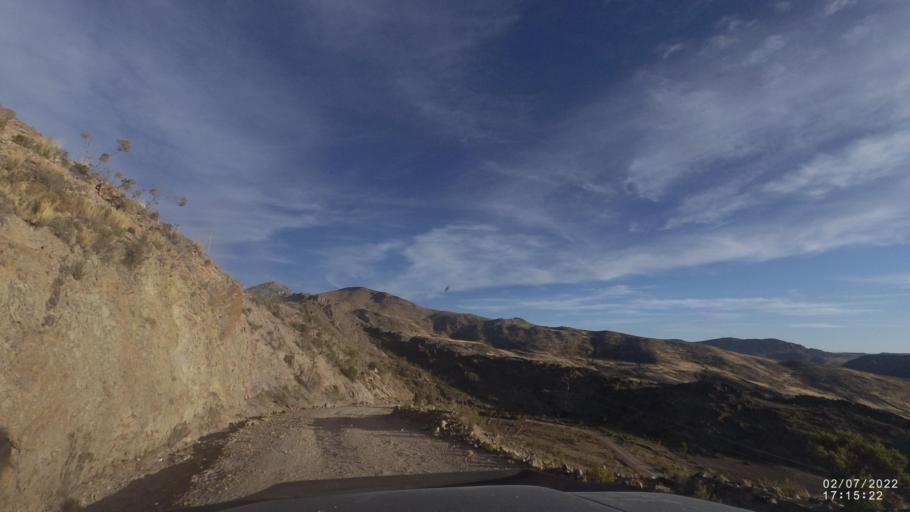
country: BO
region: Cochabamba
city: Irpa Irpa
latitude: -17.8758
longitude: -66.5835
